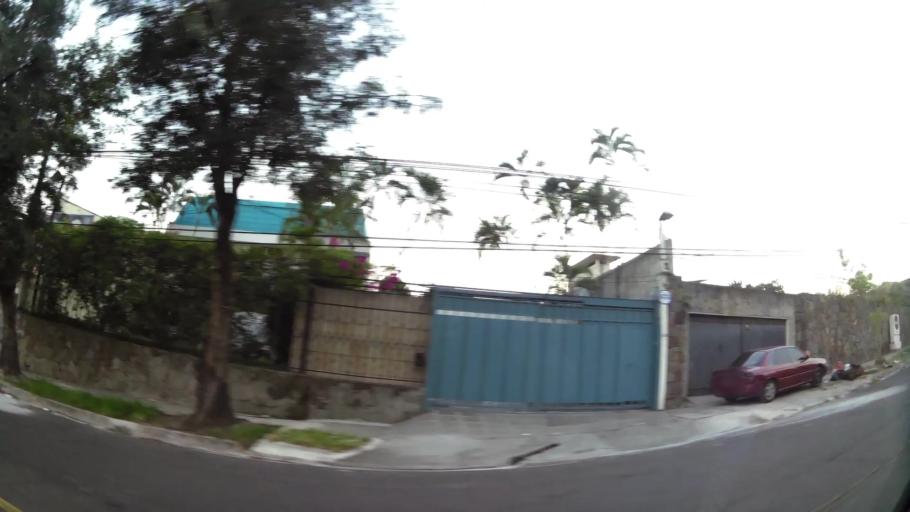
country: SV
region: La Libertad
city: Antiguo Cuscatlan
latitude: 13.6967
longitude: -89.2297
